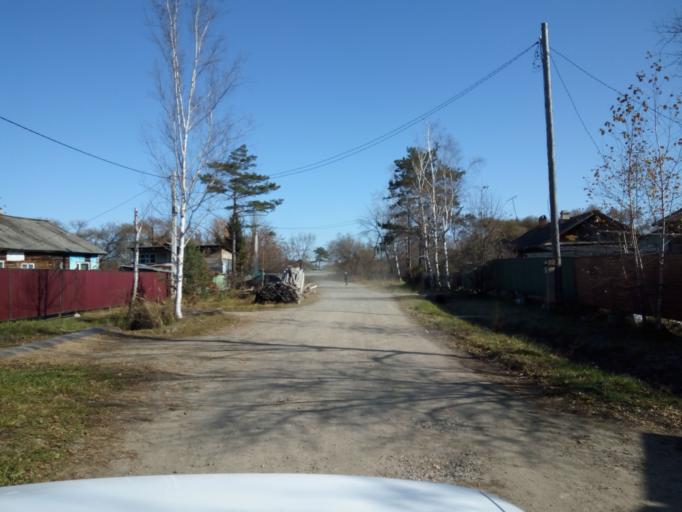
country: RU
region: Primorskiy
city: Dal'nerechensk
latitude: 45.9096
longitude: 133.8024
